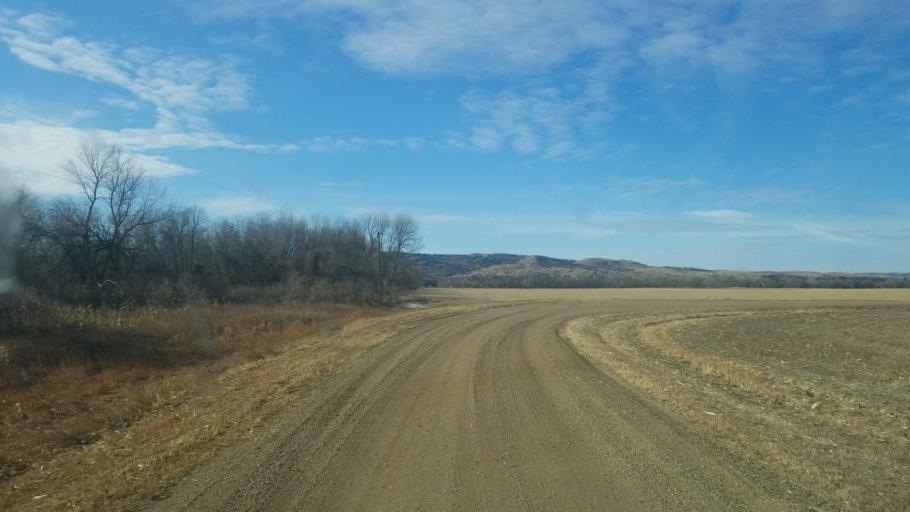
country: US
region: South Dakota
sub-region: Charles Mix County
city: Lake Andes
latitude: 42.9663
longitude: -98.4655
